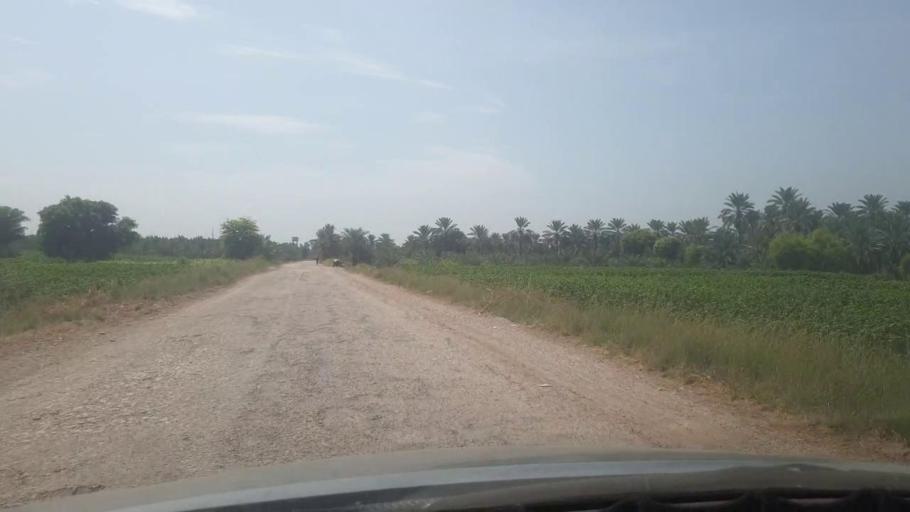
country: PK
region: Sindh
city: Bozdar
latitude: 27.2034
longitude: 68.5819
